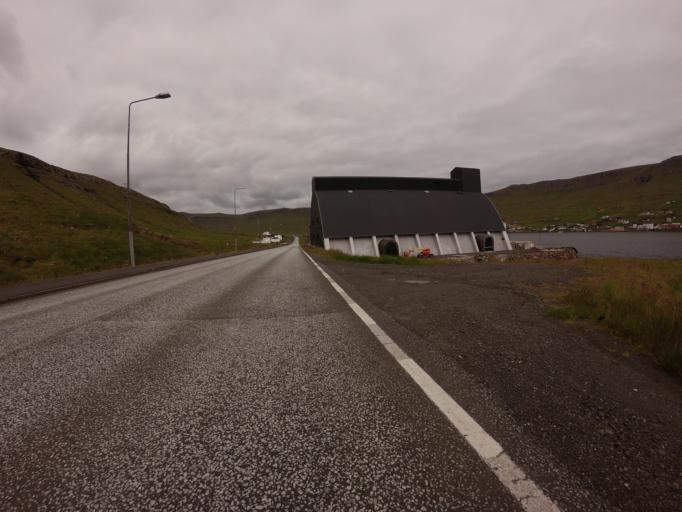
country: FO
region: Suduroy
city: Tvoroyri
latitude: 61.5514
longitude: -6.8286
